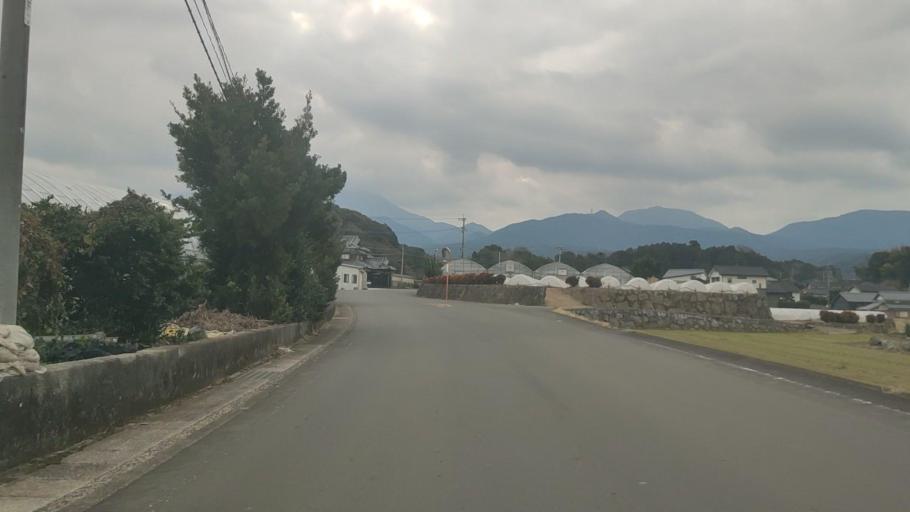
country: JP
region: Nagasaki
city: Shimabara
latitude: 32.8393
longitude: 130.2953
